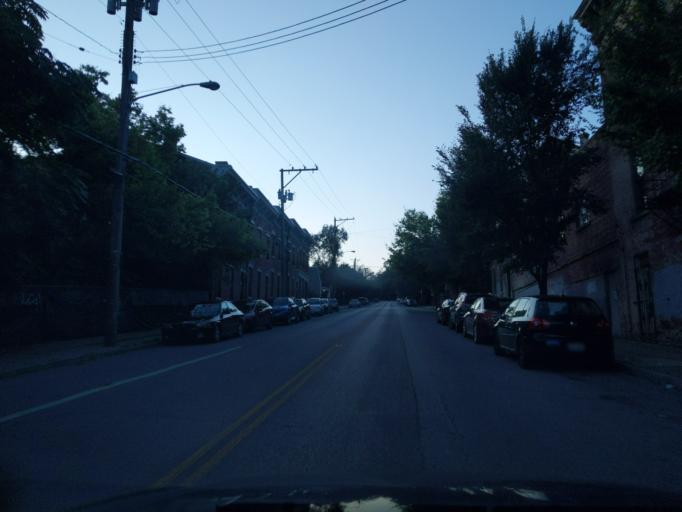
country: US
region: Kentucky
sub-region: Campbell County
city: Newport
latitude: 39.1186
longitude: -84.5176
